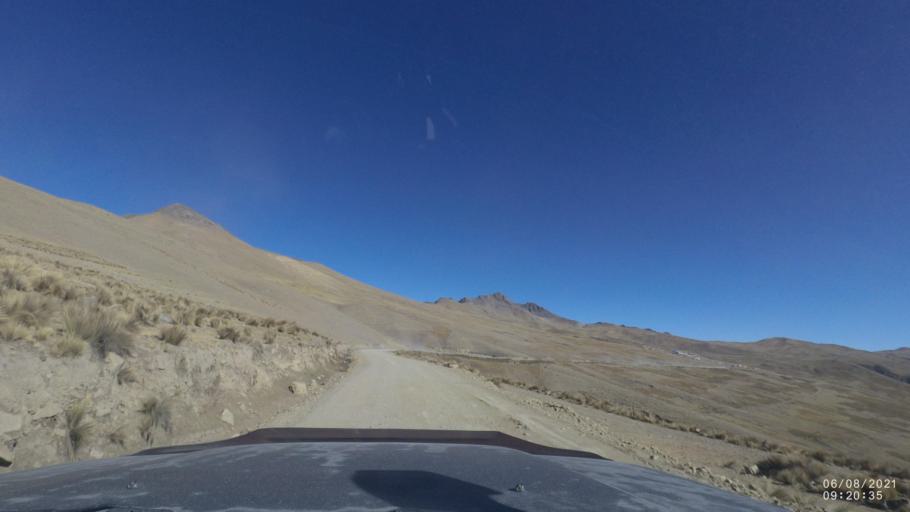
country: BO
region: Cochabamba
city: Colchani
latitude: -17.0243
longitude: -66.5401
